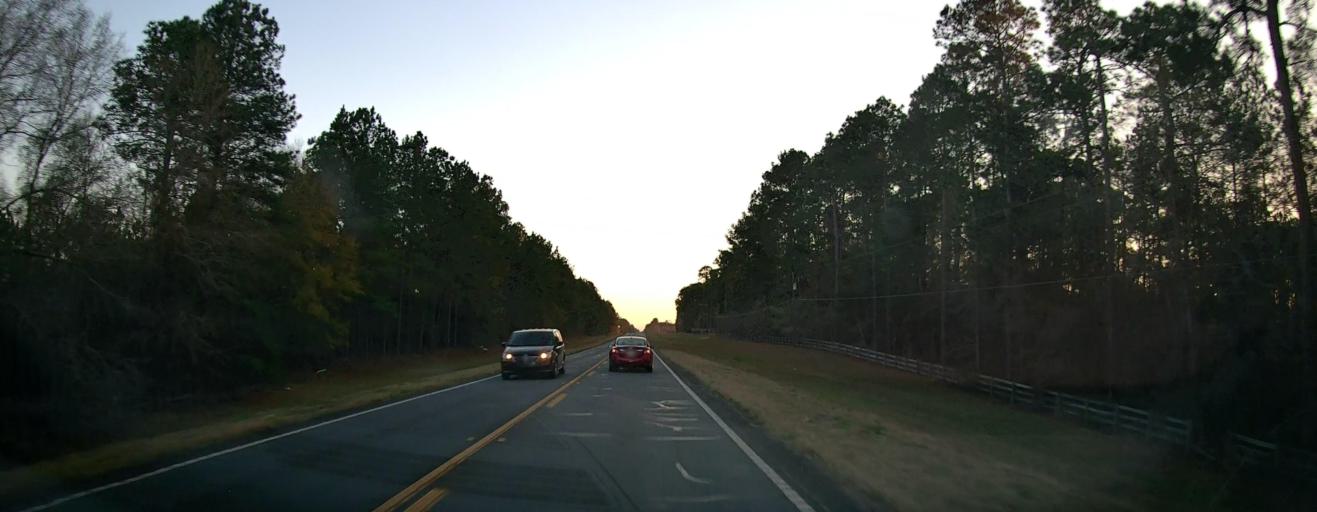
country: US
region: Georgia
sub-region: Dodge County
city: Eastman
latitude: 32.2337
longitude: -83.1504
